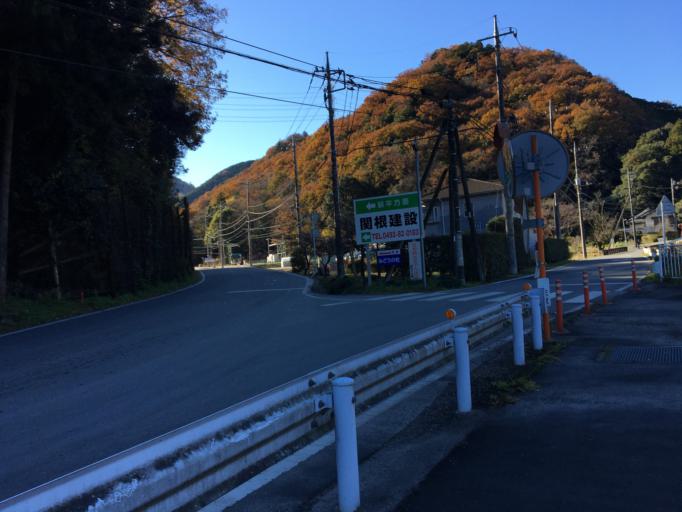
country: JP
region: Saitama
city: Yorii
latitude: 36.0543
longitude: 139.2006
